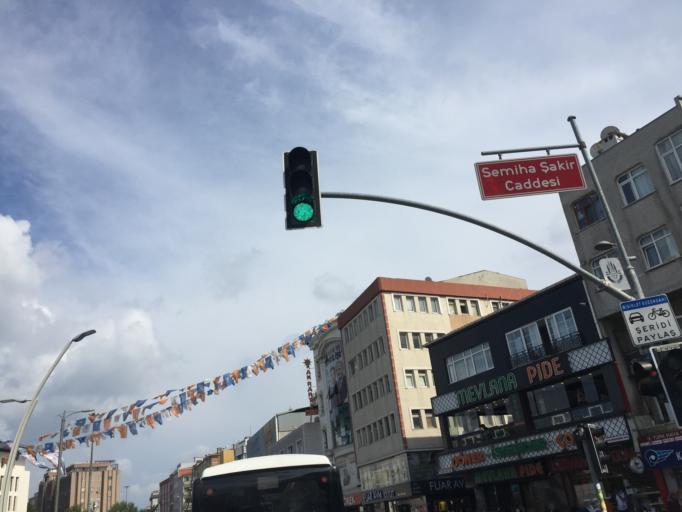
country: TR
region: Istanbul
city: Zeytinburnu
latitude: 40.9949
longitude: 28.9030
